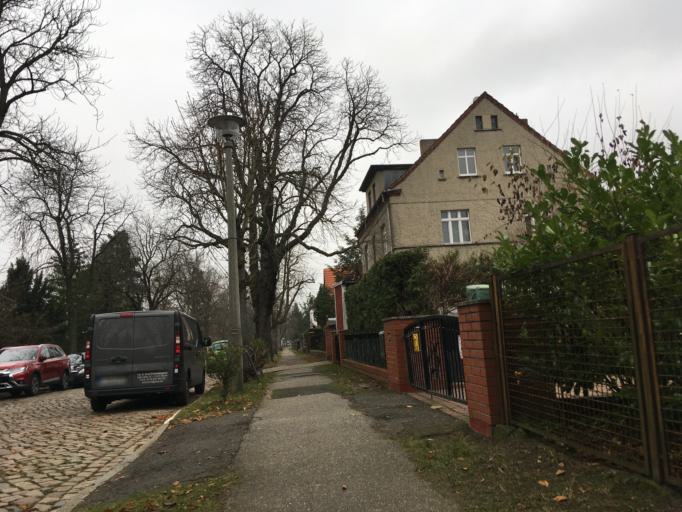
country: DE
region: Berlin
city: Buchholz
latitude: 52.6028
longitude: 13.4357
